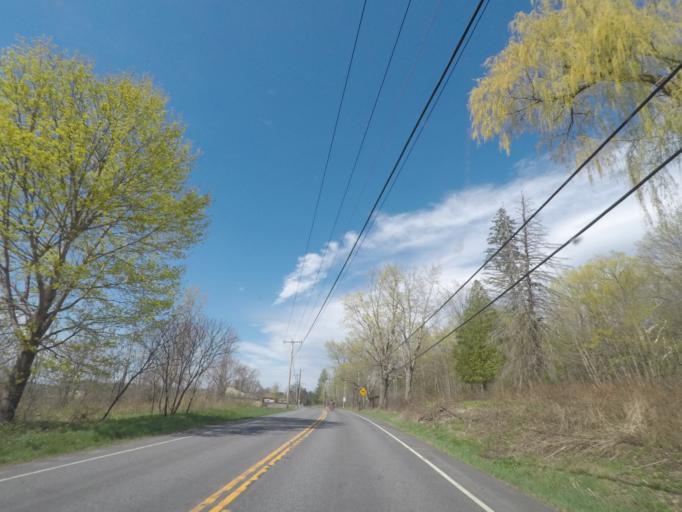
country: US
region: New York
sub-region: Greene County
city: Cairo
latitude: 42.3820
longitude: -74.0330
